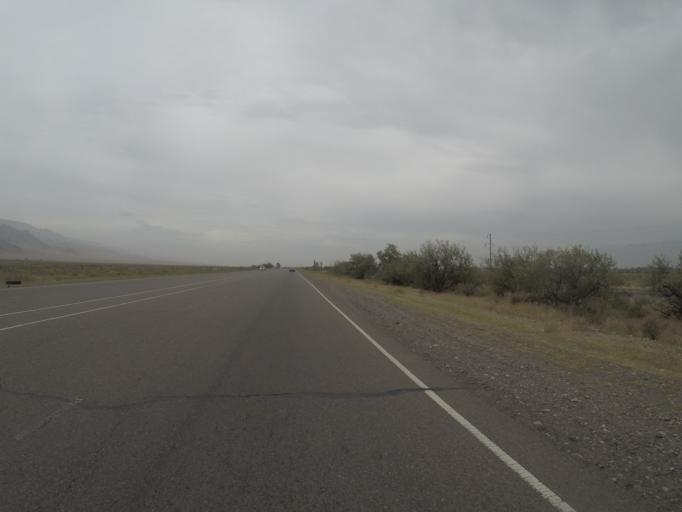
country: KG
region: Chuy
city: Tokmok
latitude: 42.8297
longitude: 75.4689
